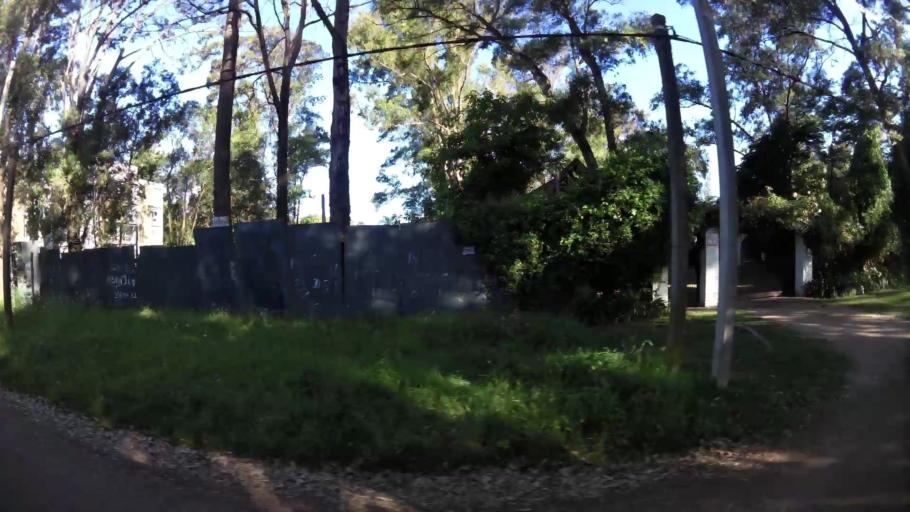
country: UY
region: Canelones
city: Paso de Carrasco
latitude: -34.8562
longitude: -56.0360
